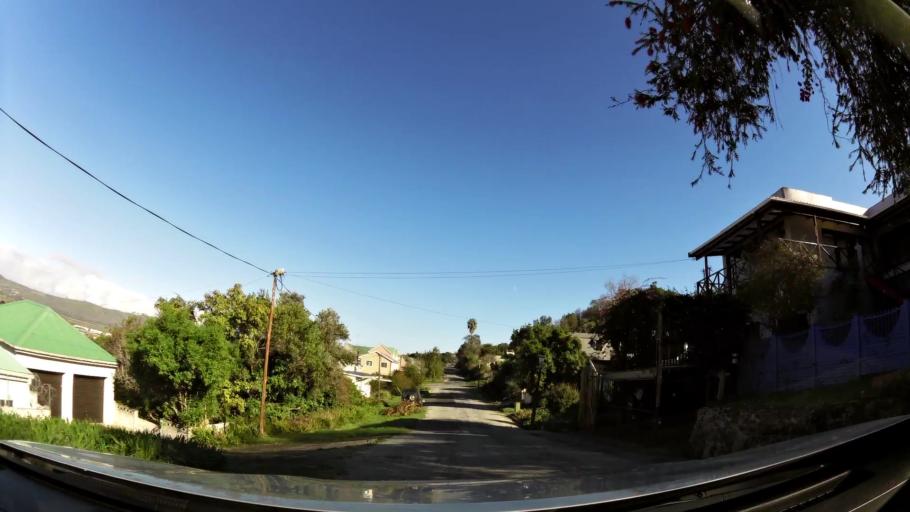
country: ZA
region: Western Cape
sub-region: Eden District Municipality
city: Knysna
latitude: -34.0327
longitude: 23.0523
